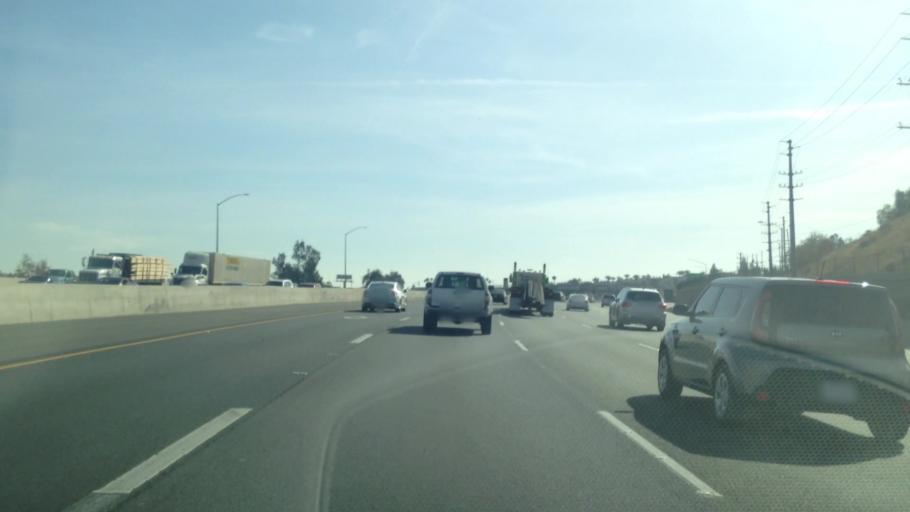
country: US
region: California
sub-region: Riverside County
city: Highgrove
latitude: 33.9534
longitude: -117.3043
